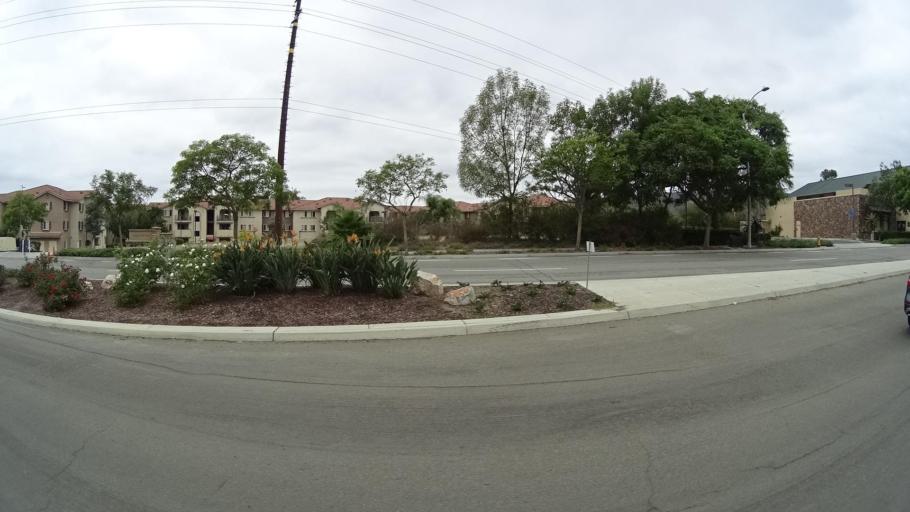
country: US
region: California
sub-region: San Diego County
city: Fairbanks Ranch
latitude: 33.0209
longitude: -117.1192
